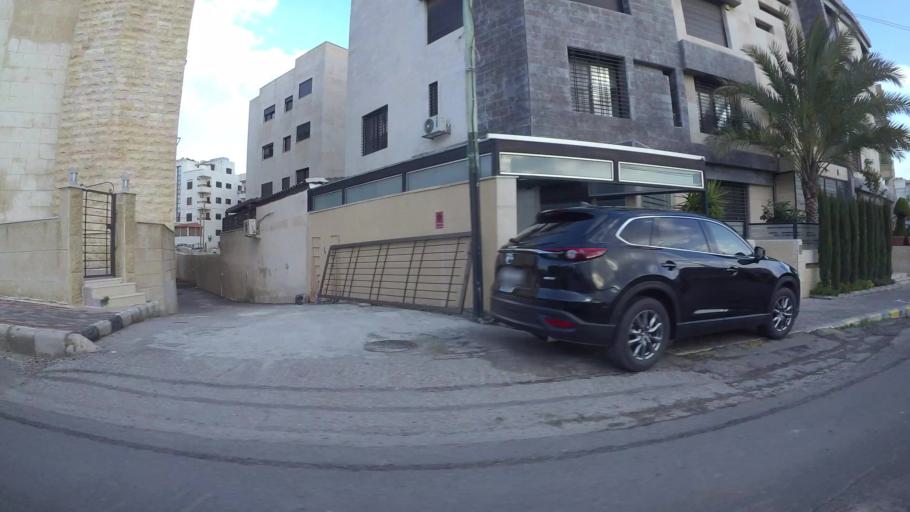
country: JO
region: Amman
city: Al Jubayhah
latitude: 31.9844
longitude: 35.8636
